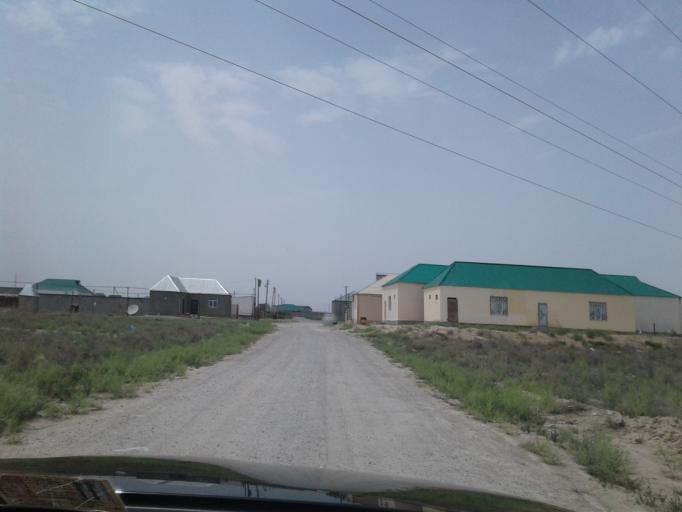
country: TM
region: Ahal
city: Ashgabat
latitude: 37.9813
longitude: 58.3189
